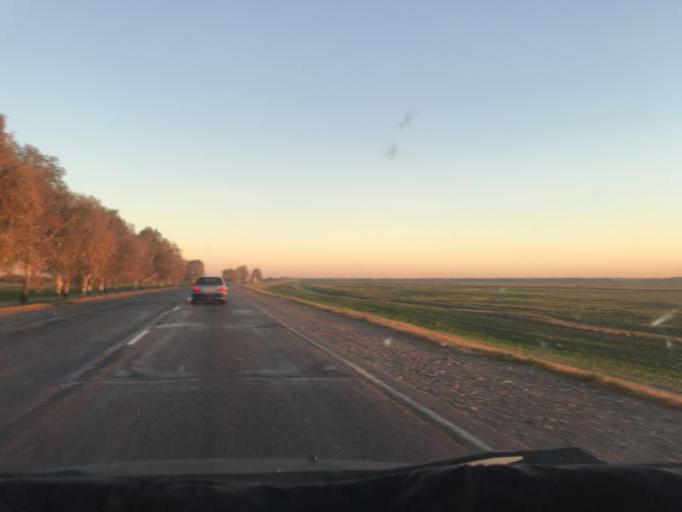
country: BY
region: Gomel
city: Kalinkavichy
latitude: 52.1557
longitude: 29.2413
